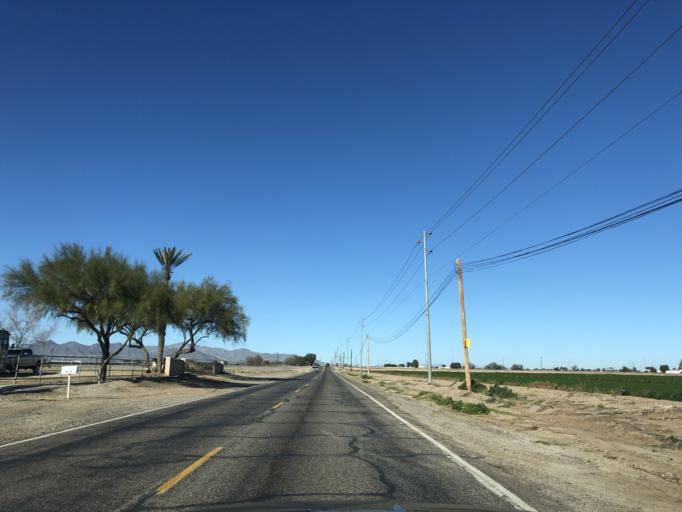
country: US
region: Arizona
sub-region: Maricopa County
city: Buckeye
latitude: 33.3886
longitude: -112.5042
